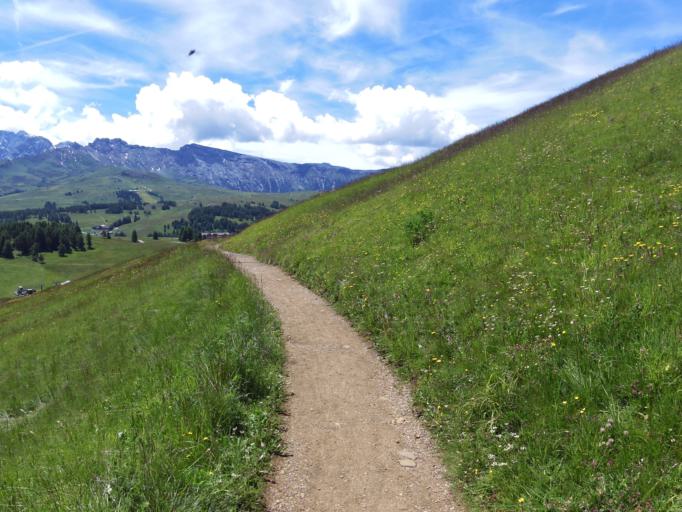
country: IT
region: Trentino-Alto Adige
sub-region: Bolzano
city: Ortisei
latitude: 46.5543
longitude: 11.6491
